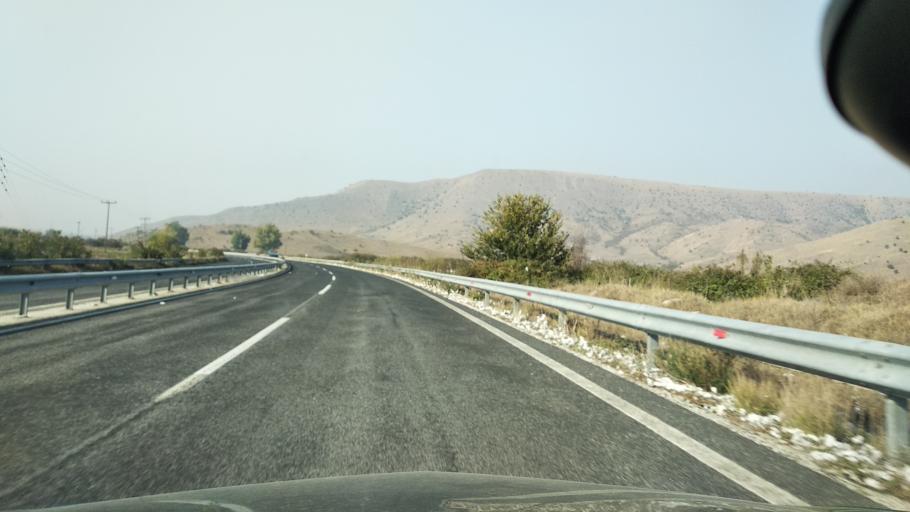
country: GR
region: Thessaly
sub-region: Trikala
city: Zarkos
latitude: 39.5975
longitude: 22.1044
